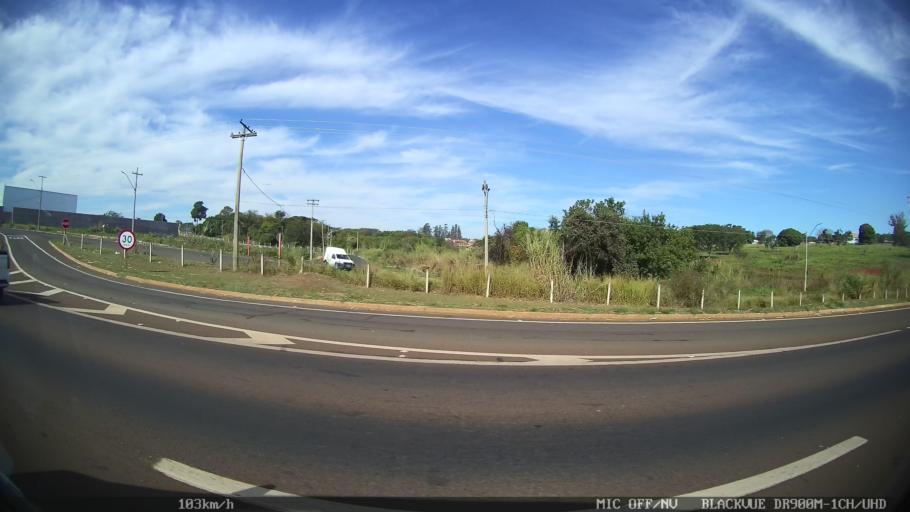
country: BR
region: Sao Paulo
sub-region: Araraquara
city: Araraquara
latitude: -21.8042
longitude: -48.1488
